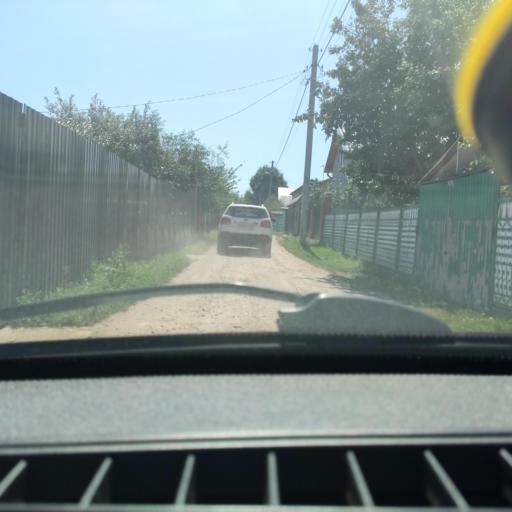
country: RU
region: Samara
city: Tol'yatti
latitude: 53.5970
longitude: 49.3059
